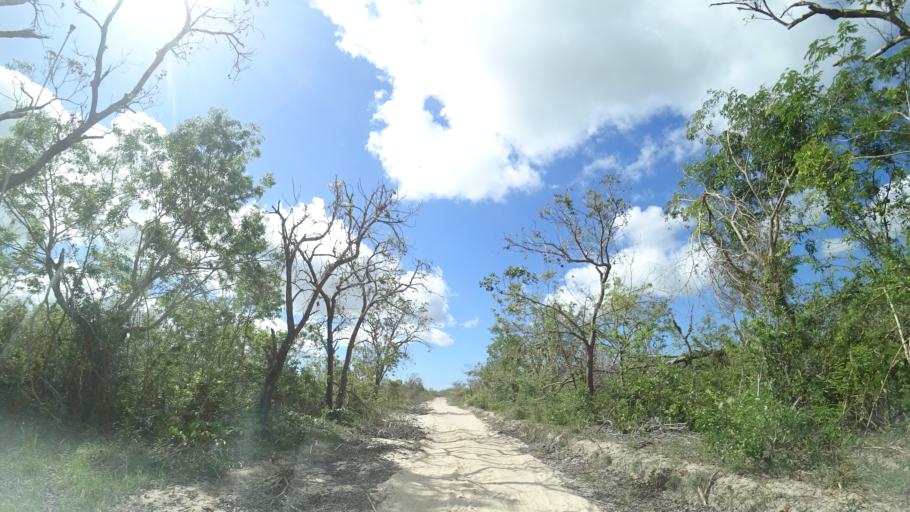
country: MZ
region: Sofala
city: Beira
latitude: -19.5784
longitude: 35.1575
